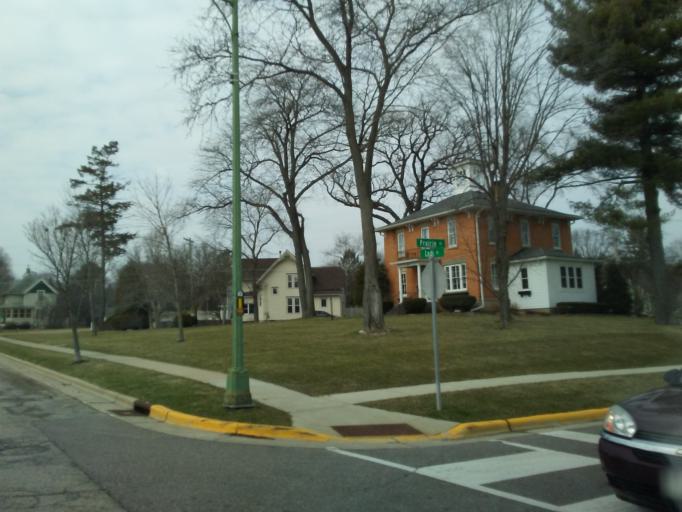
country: US
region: Wisconsin
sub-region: Columbia County
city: Lodi
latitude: 43.3129
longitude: -89.5285
